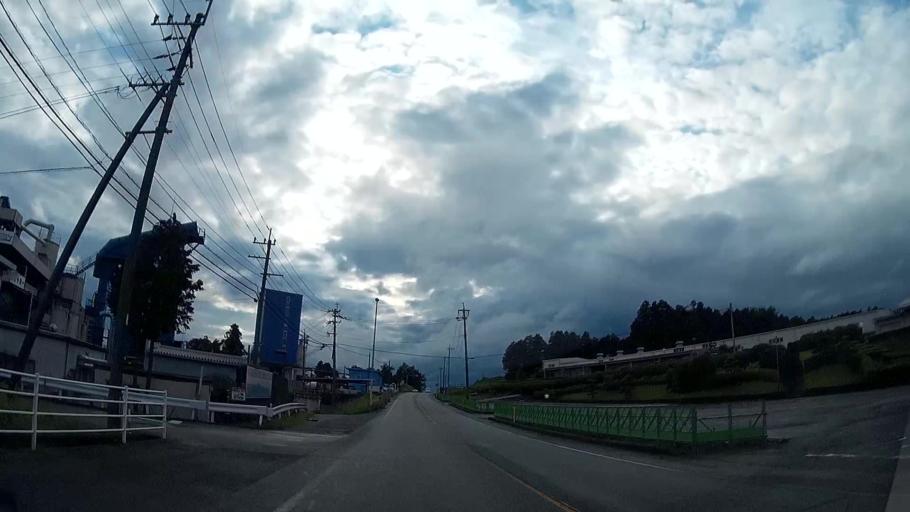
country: JP
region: Kumamoto
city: Ozu
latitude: 32.8776
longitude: 130.9184
